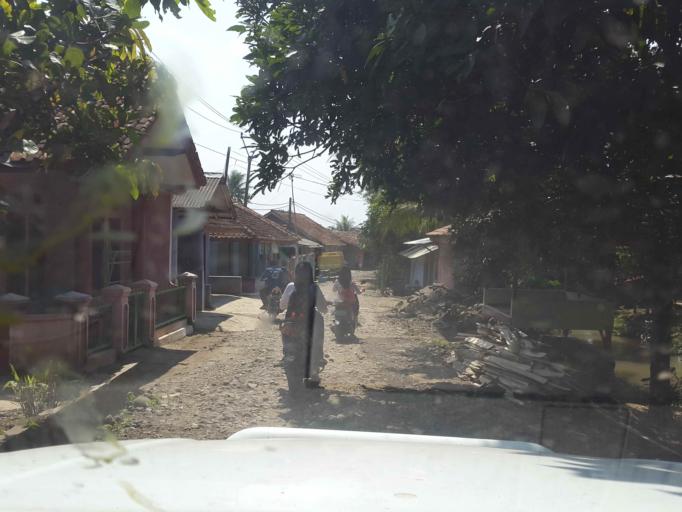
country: ID
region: West Java
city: Ciranjang-hilir
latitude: -6.9029
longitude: 107.2180
